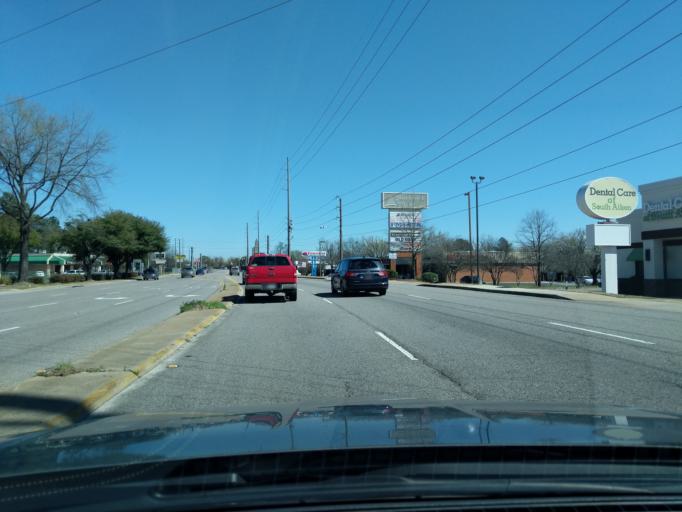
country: US
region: South Carolina
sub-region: Aiken County
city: Aiken
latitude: 33.5219
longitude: -81.7256
